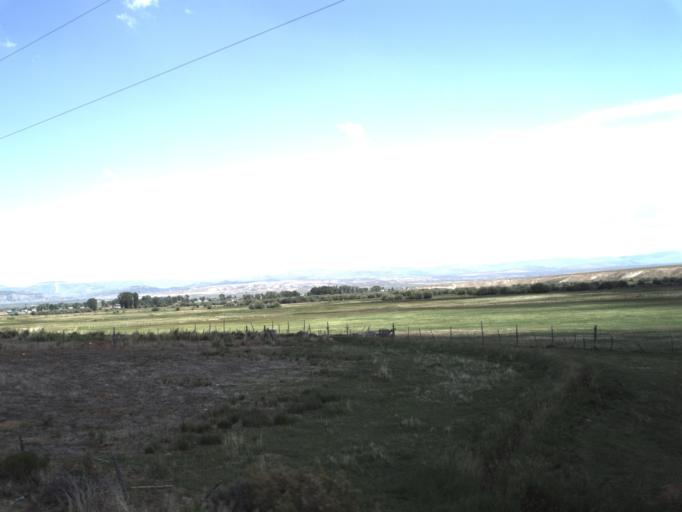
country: US
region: Utah
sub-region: Rich County
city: Randolph
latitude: 41.5202
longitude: -111.1954
